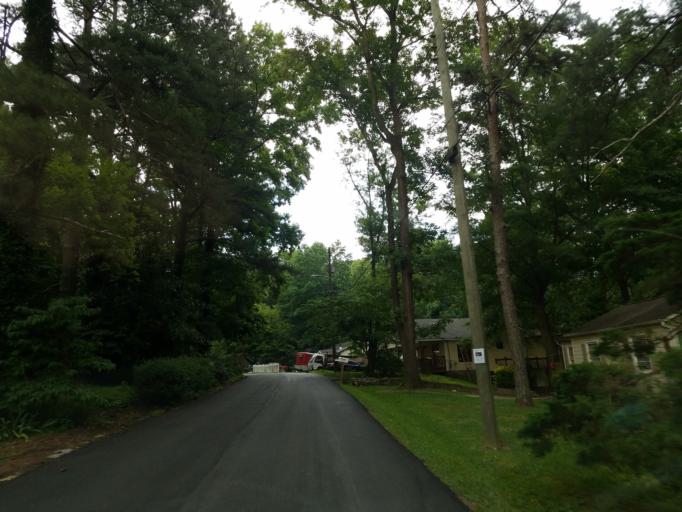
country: US
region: Georgia
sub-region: Cobb County
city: Fair Oaks
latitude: 33.9299
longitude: -84.5470
